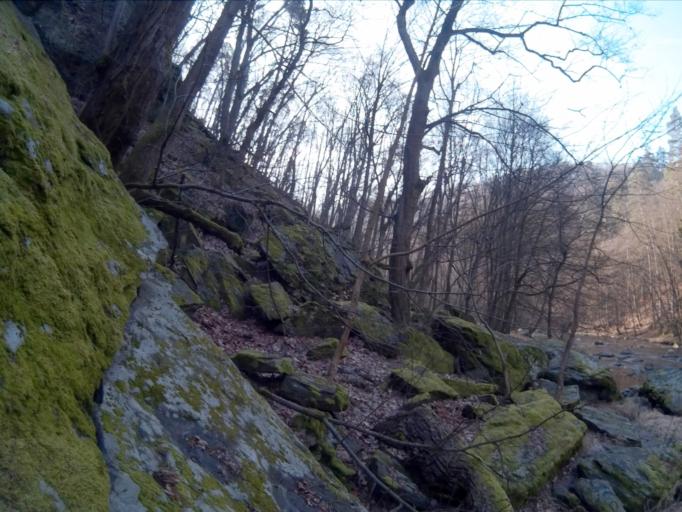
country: CZ
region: Vysocina
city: Namest' nad Oslavou
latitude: 49.1719
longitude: 16.1644
